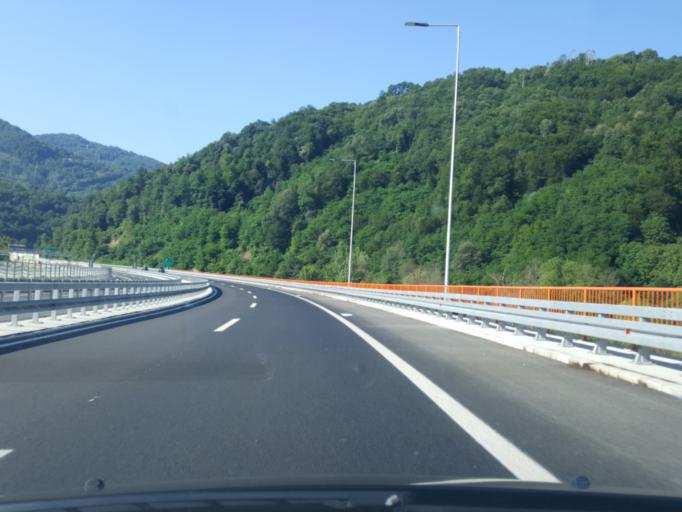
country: RS
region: Central Serbia
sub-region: Jablanicki Okrug
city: Vlasotince
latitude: 42.8335
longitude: 22.1280
